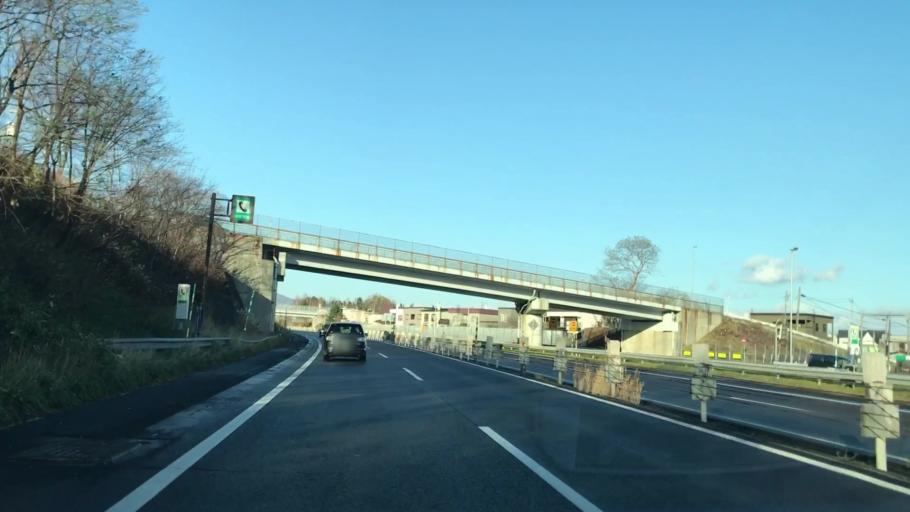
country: JP
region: Hokkaido
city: Sapporo
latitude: 43.1245
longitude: 141.2108
